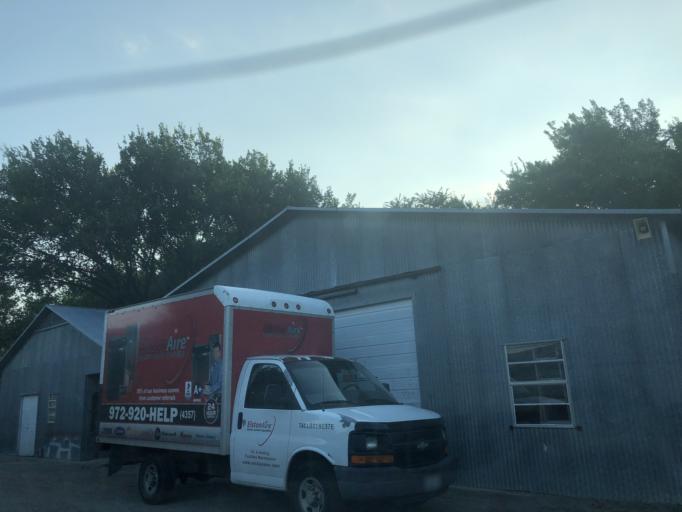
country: US
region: Texas
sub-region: Dallas County
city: Sunnyvale
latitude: 32.8392
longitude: -96.5669
